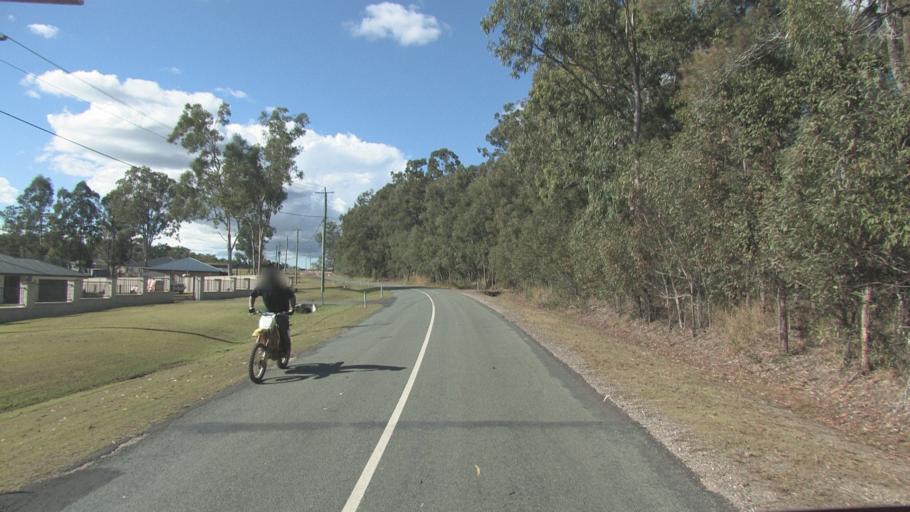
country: AU
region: Queensland
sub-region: Logan
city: Chambers Flat
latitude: -27.7893
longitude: 153.0975
